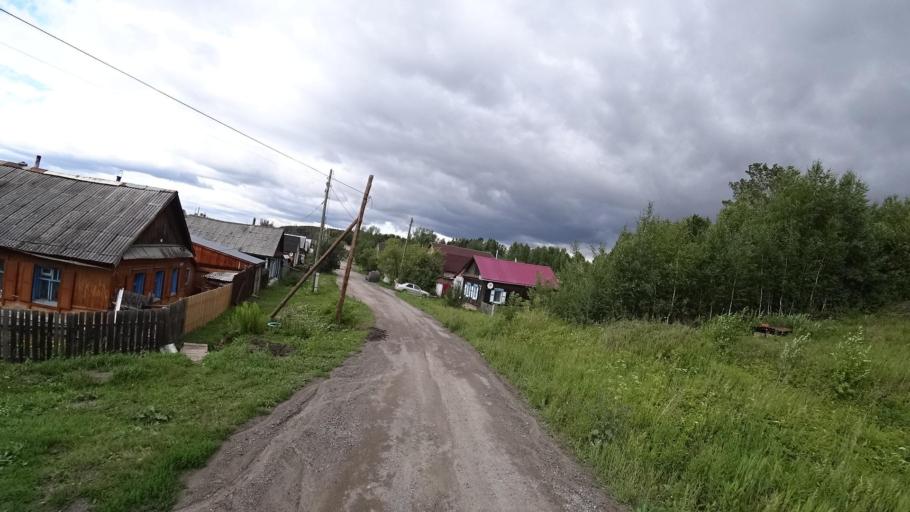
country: RU
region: Sverdlovsk
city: Kamyshlov
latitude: 56.8567
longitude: 62.7184
